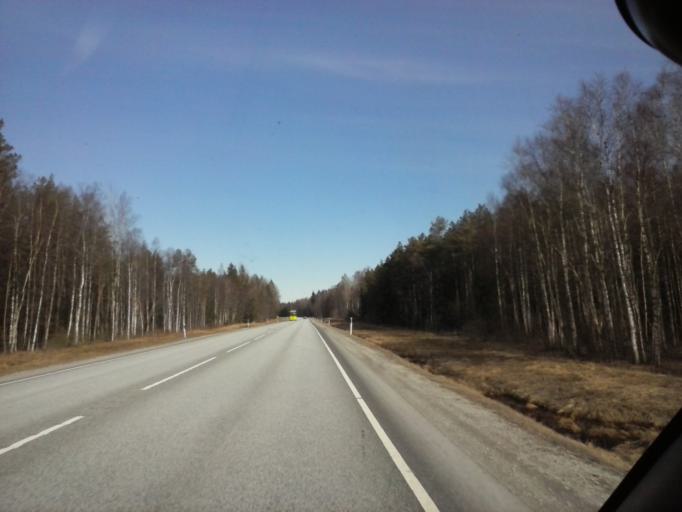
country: EE
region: Jaervamaa
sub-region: Paide linn
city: Paide
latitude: 59.0706
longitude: 25.4287
